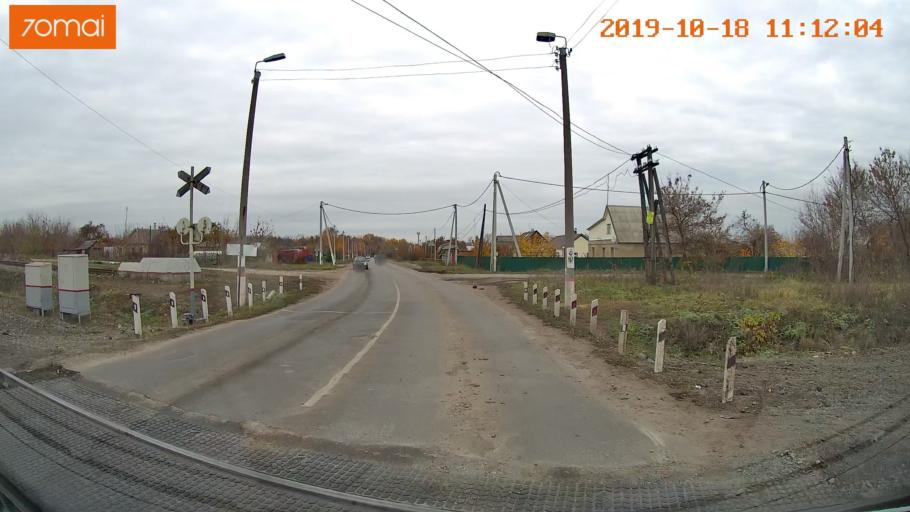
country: RU
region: Tula
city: Kimovsk
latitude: 53.9629
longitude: 38.5517
